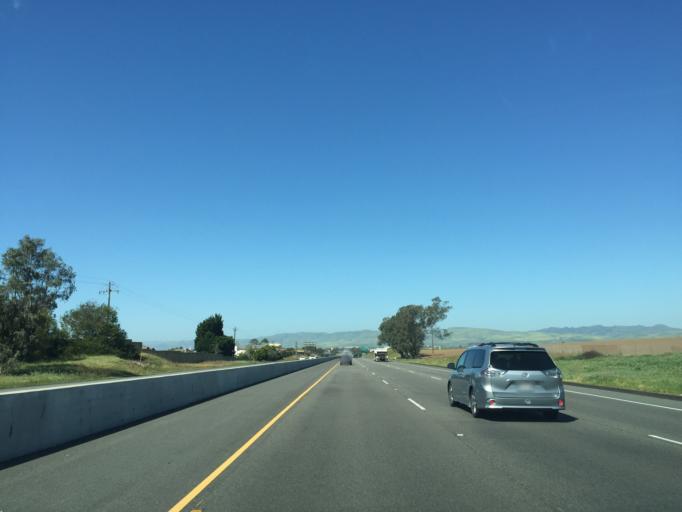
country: US
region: California
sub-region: Santa Barbara County
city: Orcutt
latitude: 34.9012
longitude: -120.4181
